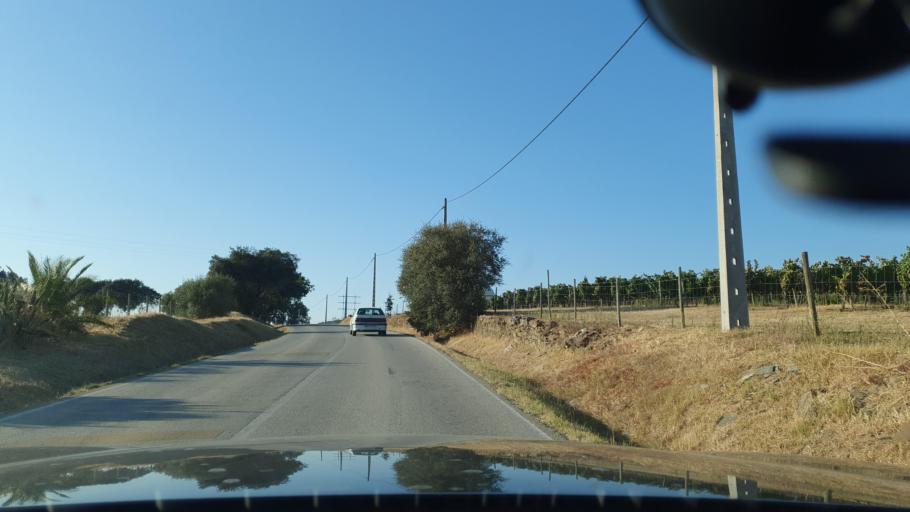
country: PT
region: Evora
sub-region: Estremoz
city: Estremoz
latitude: 38.8613
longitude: -7.6190
